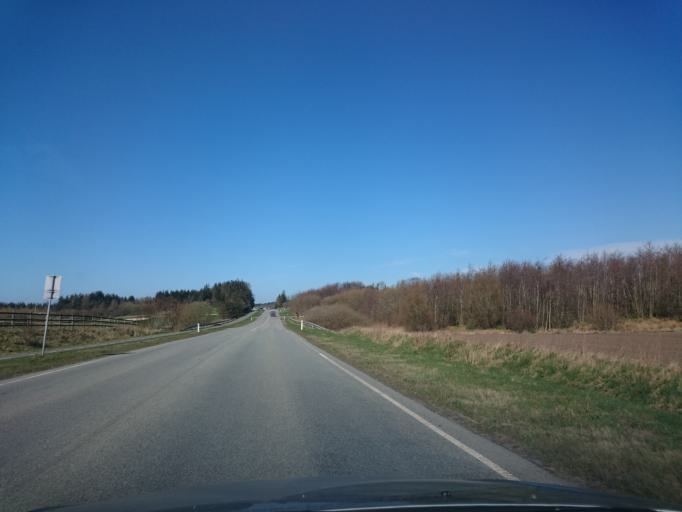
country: DK
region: North Denmark
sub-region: Hjorring Kommune
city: Hjorring
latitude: 57.4929
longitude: 10.0015
